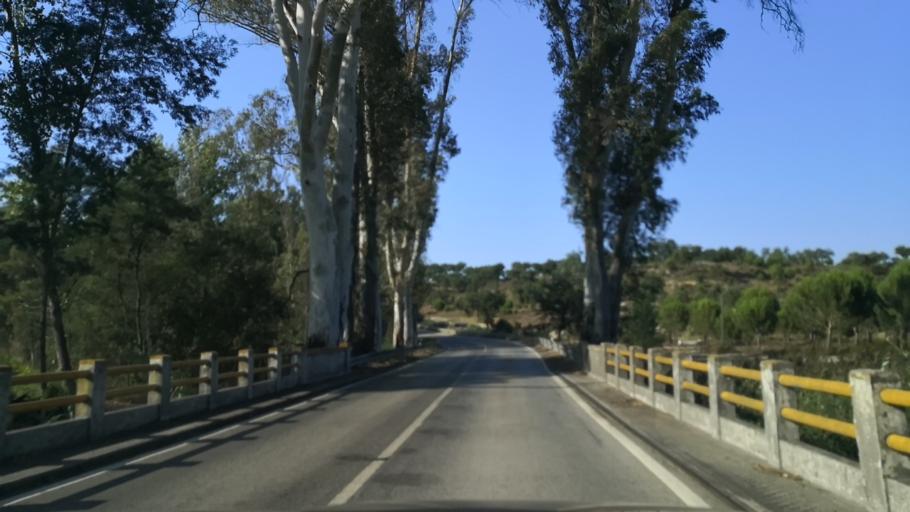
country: PT
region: Santarem
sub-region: Almeirim
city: Fazendas de Almeirim
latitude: 39.0649
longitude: -8.5649
